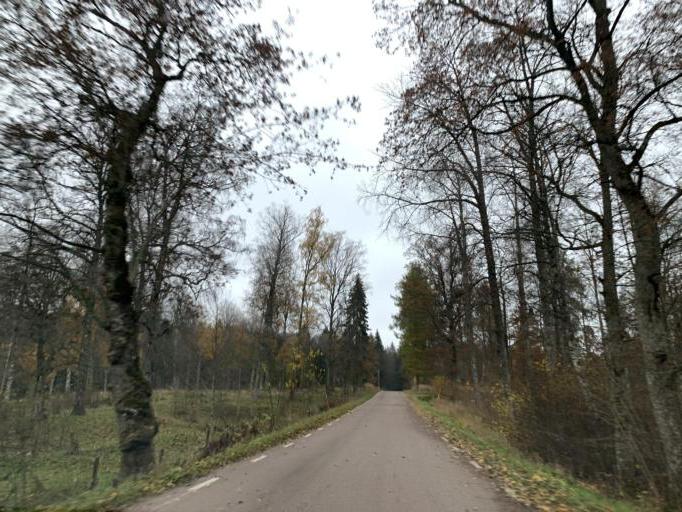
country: SE
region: Vaestmanland
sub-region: Surahammars Kommun
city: Ramnas
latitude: 59.6940
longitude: 16.0769
